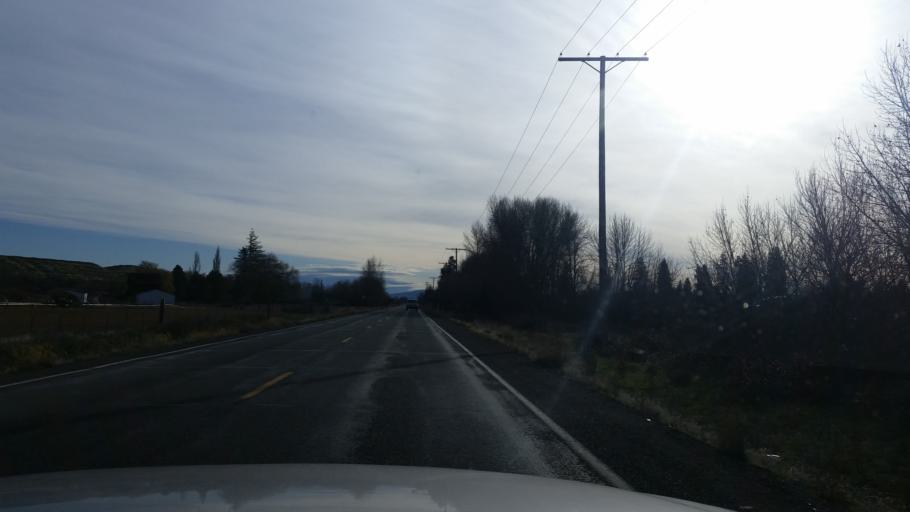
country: US
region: Washington
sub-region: Kittitas County
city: Ellensburg
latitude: 47.0548
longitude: -120.6405
